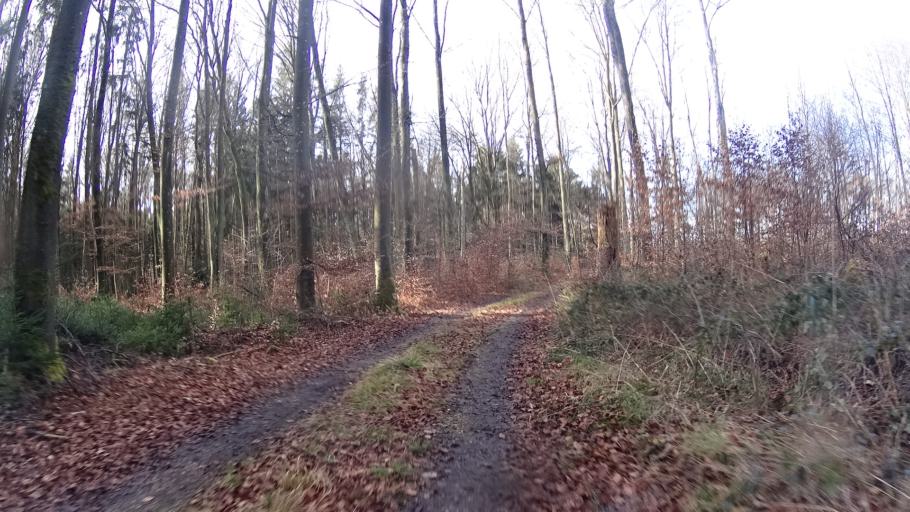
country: DE
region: Bavaria
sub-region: Upper Bavaria
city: Walting
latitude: 48.8869
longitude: 11.2782
